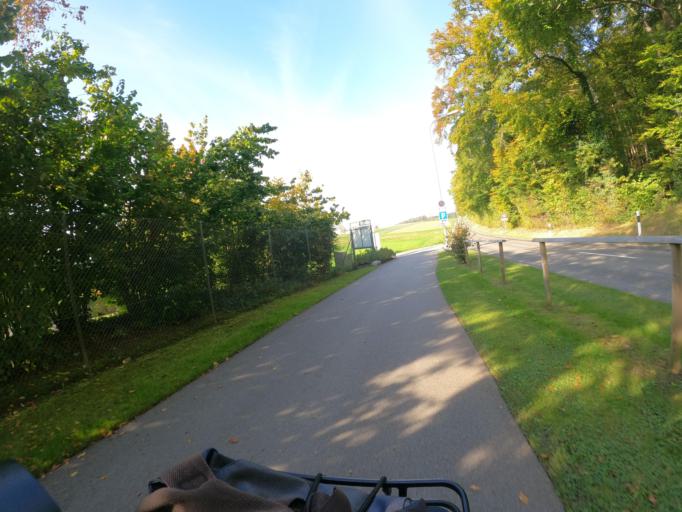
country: CH
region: Aargau
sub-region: Bezirk Muri
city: Muri
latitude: 47.2825
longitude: 8.3452
